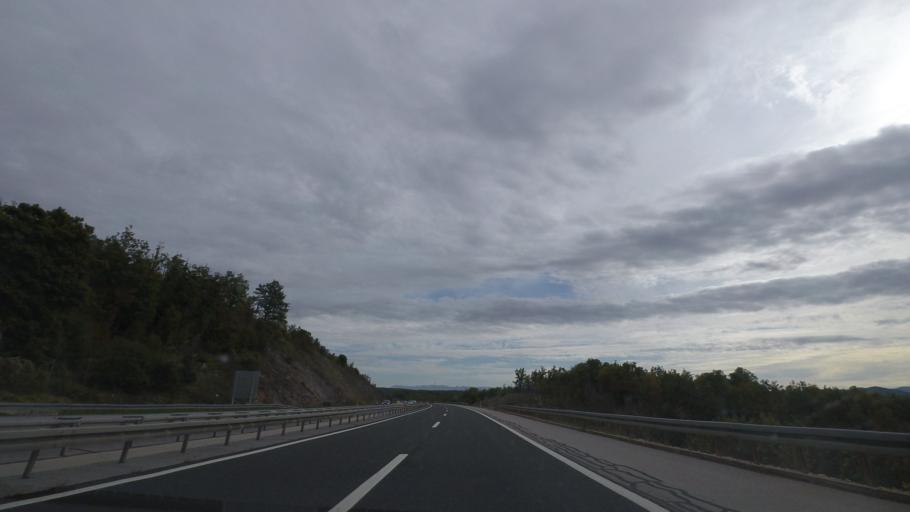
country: HR
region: Licko-Senjska
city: Otocac
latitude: 44.7399
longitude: 15.3785
